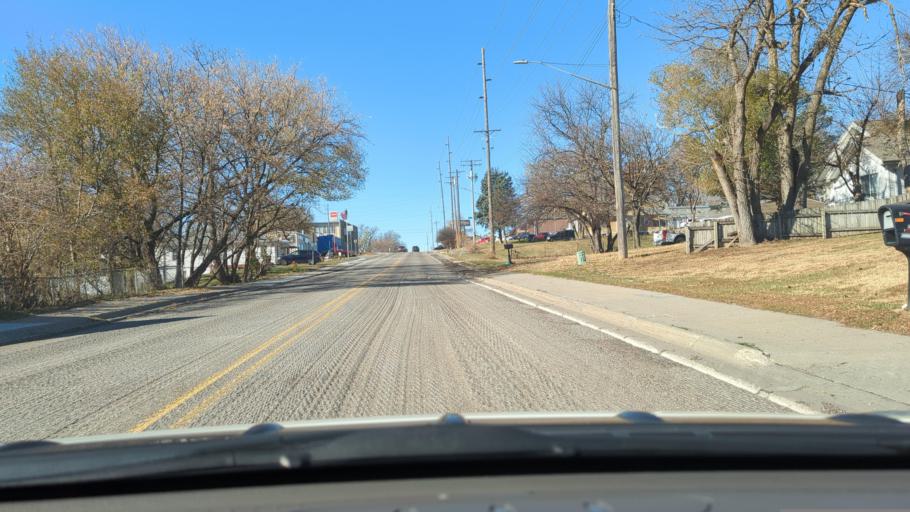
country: US
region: Nebraska
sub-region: Sarpy County
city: La Vista
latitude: 41.2053
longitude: -95.9937
